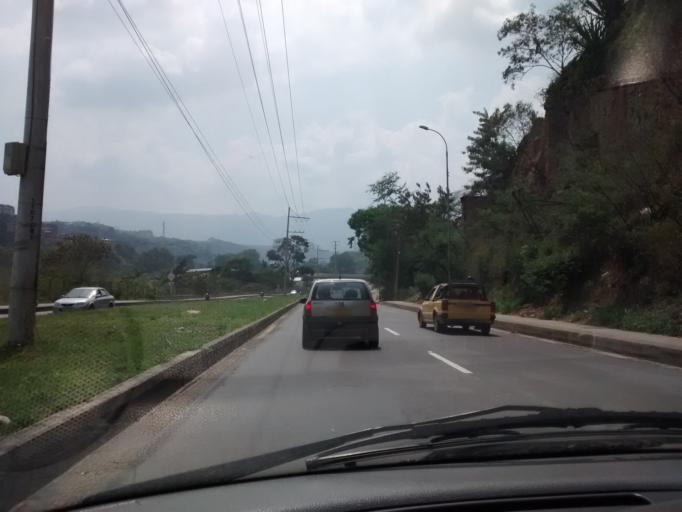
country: CO
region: Santander
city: Bucaramanga
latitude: 7.0932
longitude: -73.1220
